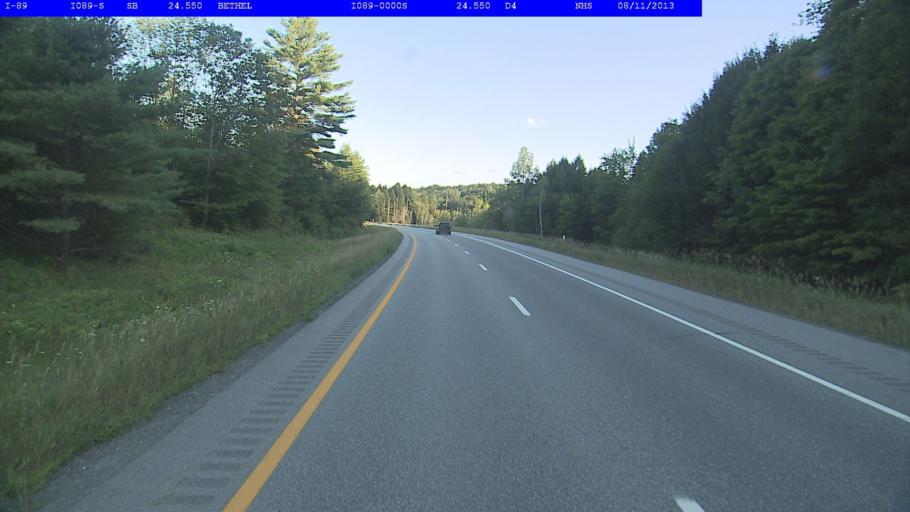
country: US
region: Vermont
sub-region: Orange County
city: Randolph
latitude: 43.8551
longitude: -72.6072
